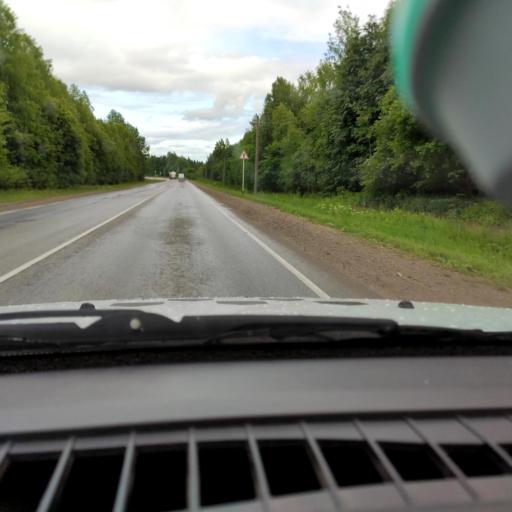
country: RU
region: Perm
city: Novyye Lyady
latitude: 58.2912
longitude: 56.6917
